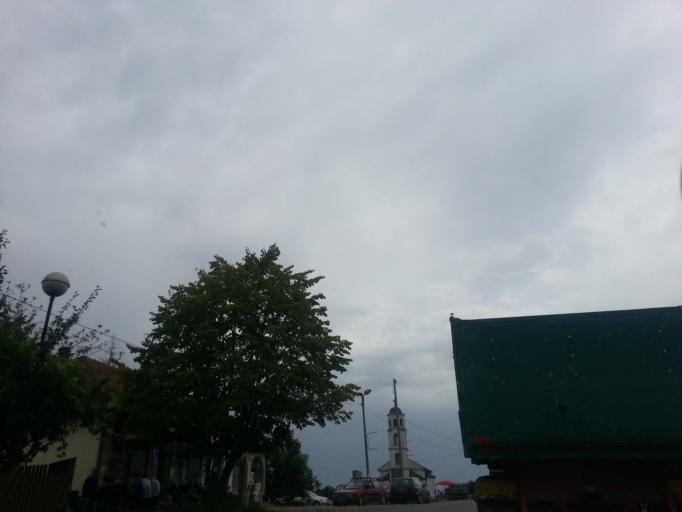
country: BA
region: Republika Srpska
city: Velika Obarska
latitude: 44.8103
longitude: 19.0662
